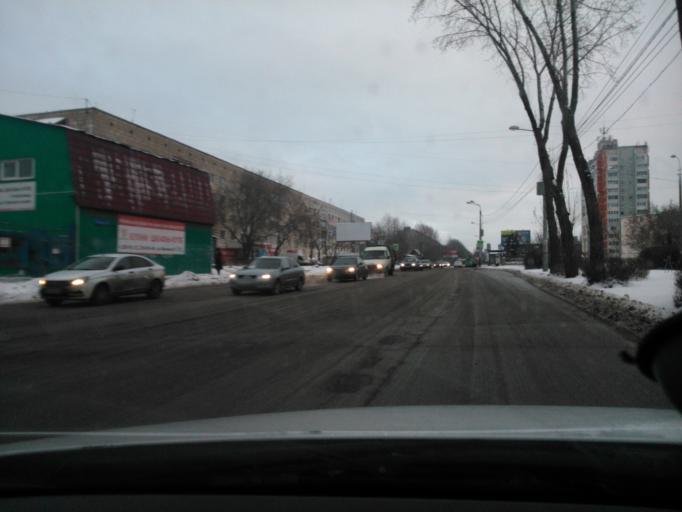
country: RU
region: Perm
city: Kondratovo
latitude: 57.9683
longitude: 56.1737
